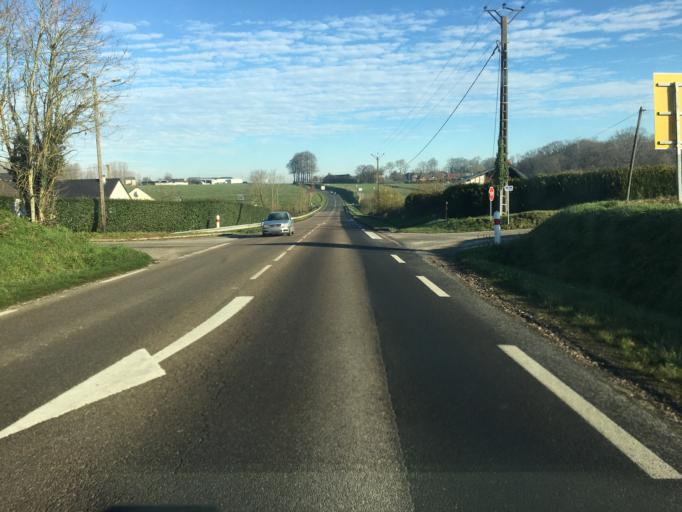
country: FR
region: Haute-Normandie
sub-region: Departement de la Seine-Maritime
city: Sainte-Marie-des-Champs
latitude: 49.6142
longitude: 0.7832
